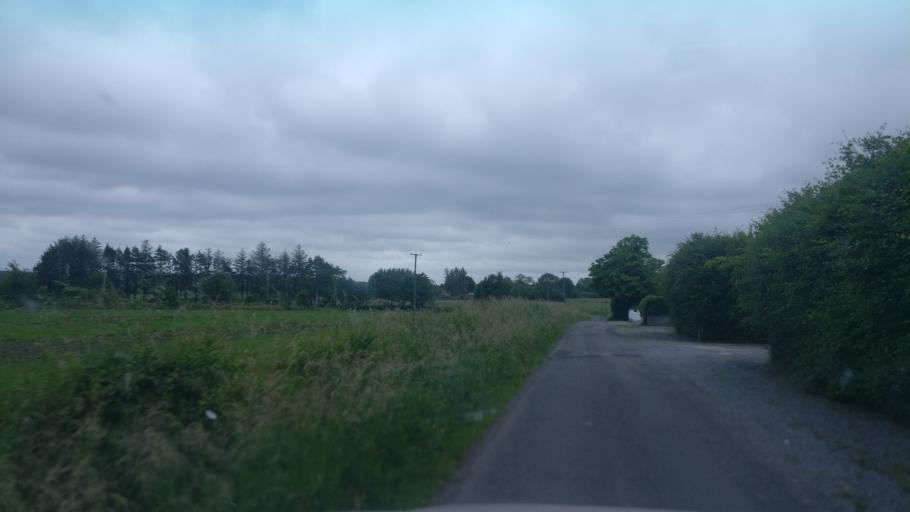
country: IE
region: Connaught
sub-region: County Galway
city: Ballinasloe
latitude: 53.3045
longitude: -8.3517
